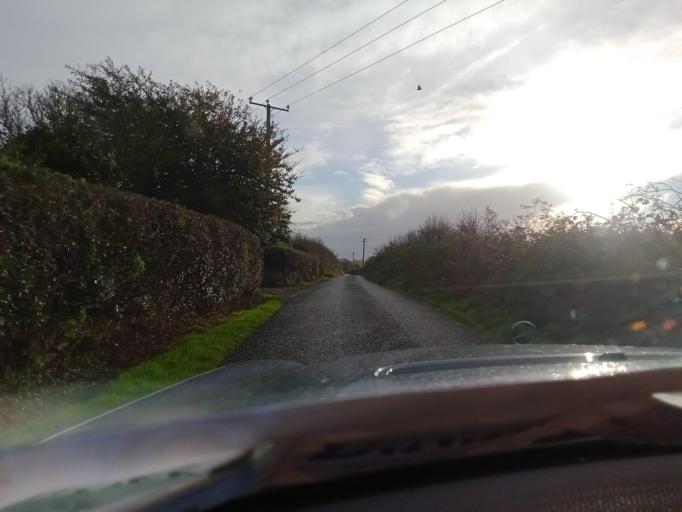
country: IE
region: Leinster
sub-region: Kilkenny
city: Mooncoin
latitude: 52.2779
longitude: -7.1885
